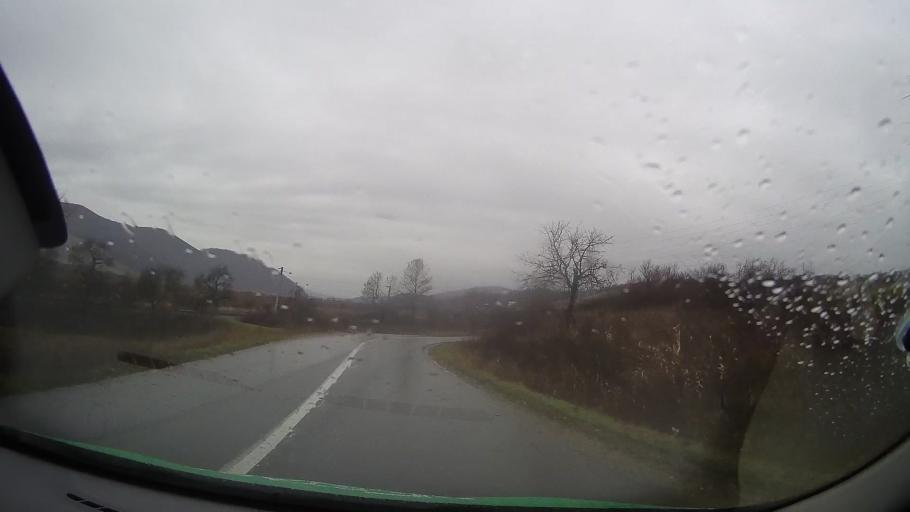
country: RO
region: Bistrita-Nasaud
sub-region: Comuna Mariselu
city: Mariselu
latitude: 47.0456
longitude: 24.4652
